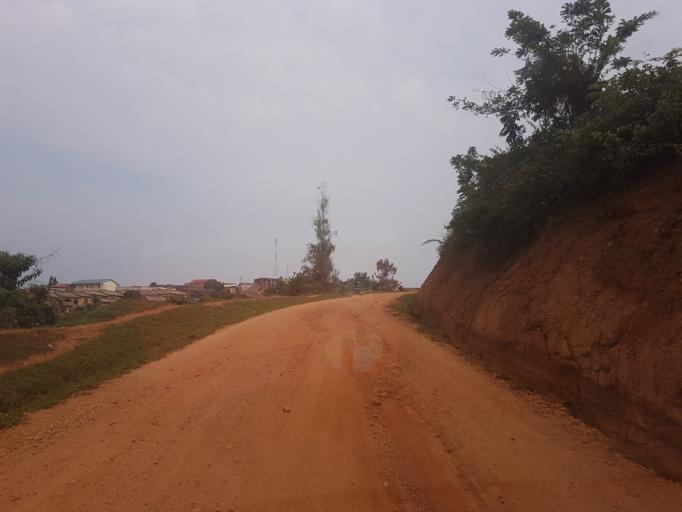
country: UG
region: Western Region
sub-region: Kanungu District
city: Kanungu
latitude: -0.8969
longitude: 29.7791
